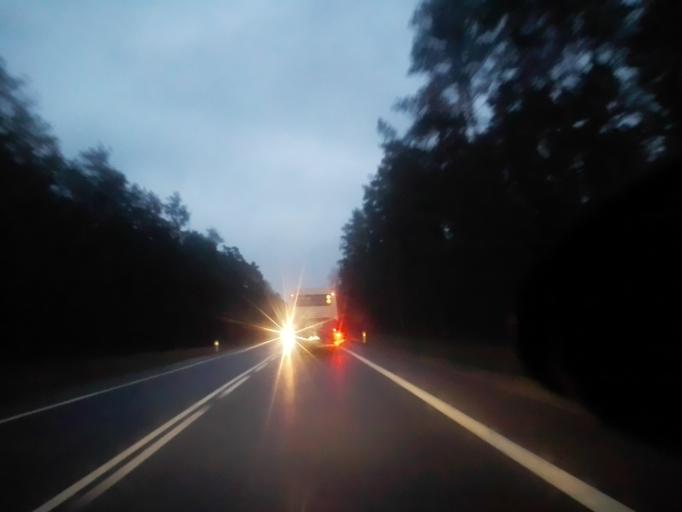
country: PL
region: Masovian Voivodeship
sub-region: Powiat wyszkowski
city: Dlugosiodlo
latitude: 52.7077
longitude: 21.6830
